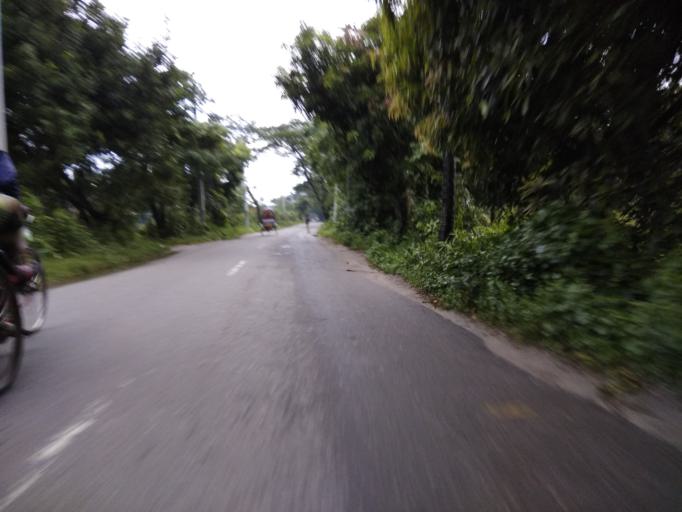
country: BD
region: Dhaka
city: Azimpur
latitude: 23.6730
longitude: 90.3056
